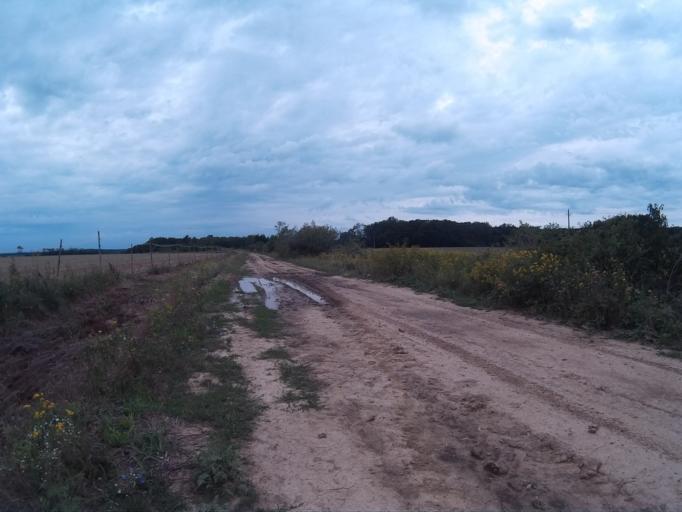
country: HU
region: Zala
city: Zalalovo
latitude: 46.7743
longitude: 16.5202
